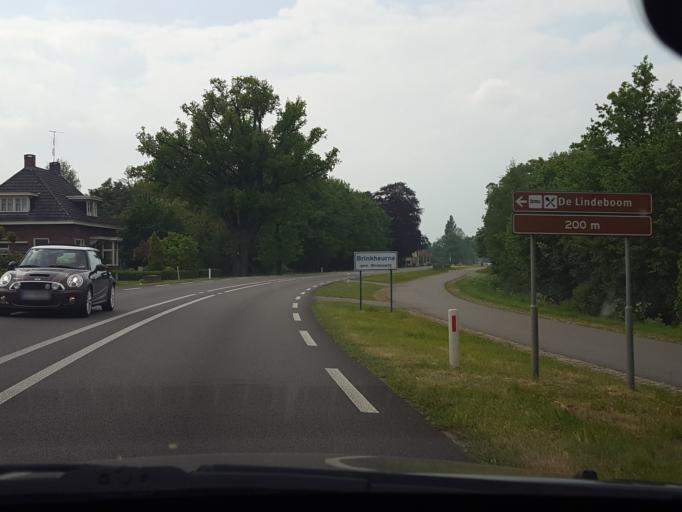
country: NL
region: Gelderland
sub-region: Gemeente Winterswijk
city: Winterswijk
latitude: 51.9496
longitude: 6.7617
